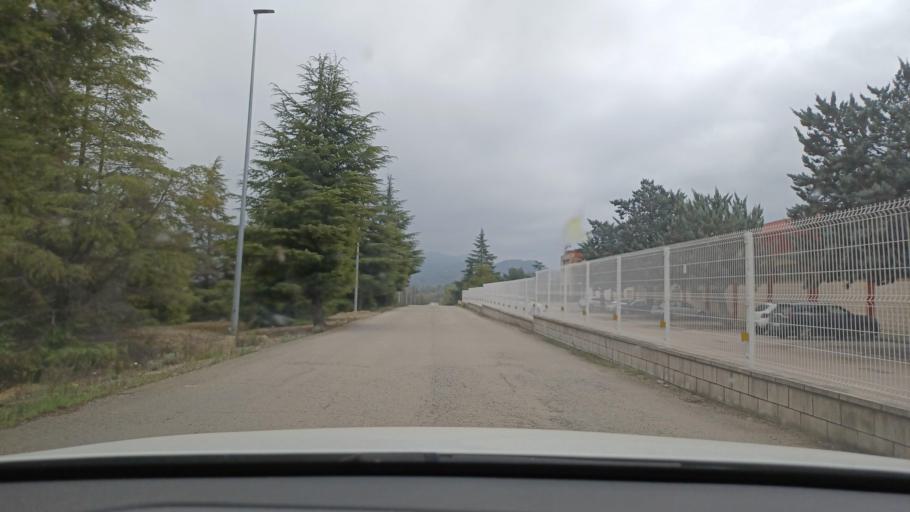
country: ES
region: Valencia
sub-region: Provincia de Valencia
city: Agullent
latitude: 38.8320
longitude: -0.5623
